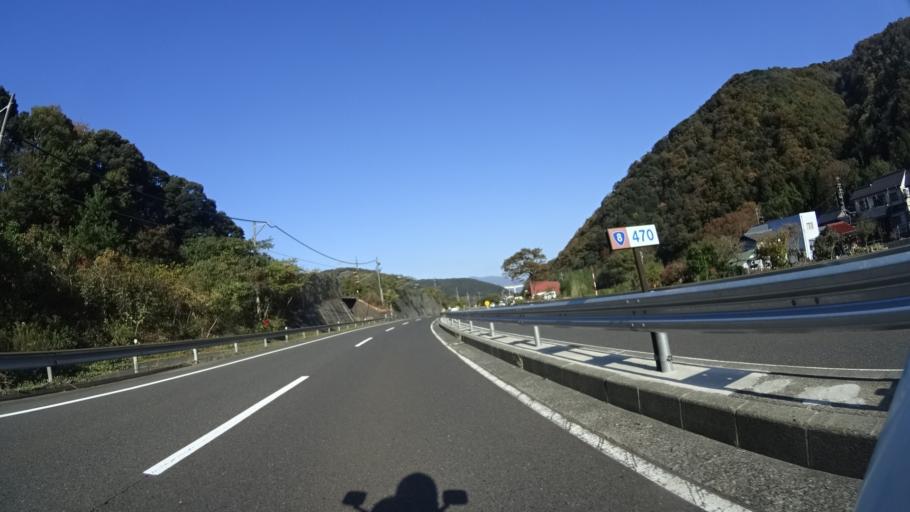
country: JP
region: Fukui
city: Tsuruga
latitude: 35.6066
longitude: 136.0890
